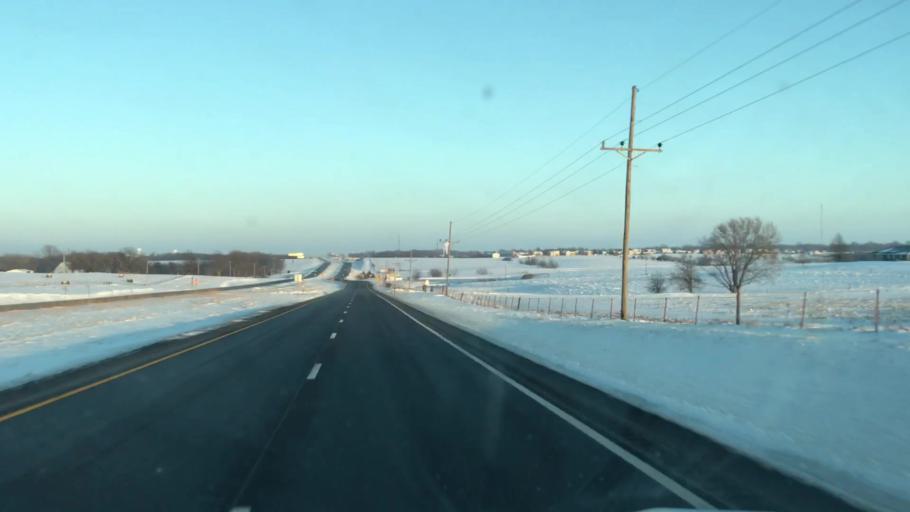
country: US
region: Missouri
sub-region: Clinton County
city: Cameron
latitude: 39.7539
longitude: -94.2734
